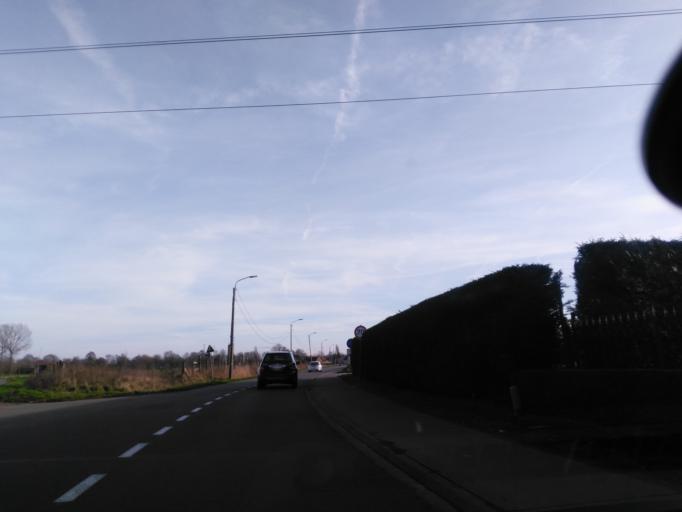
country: BE
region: Flanders
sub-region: Provincie Oost-Vlaanderen
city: Beveren
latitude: 51.2217
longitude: 4.2337
